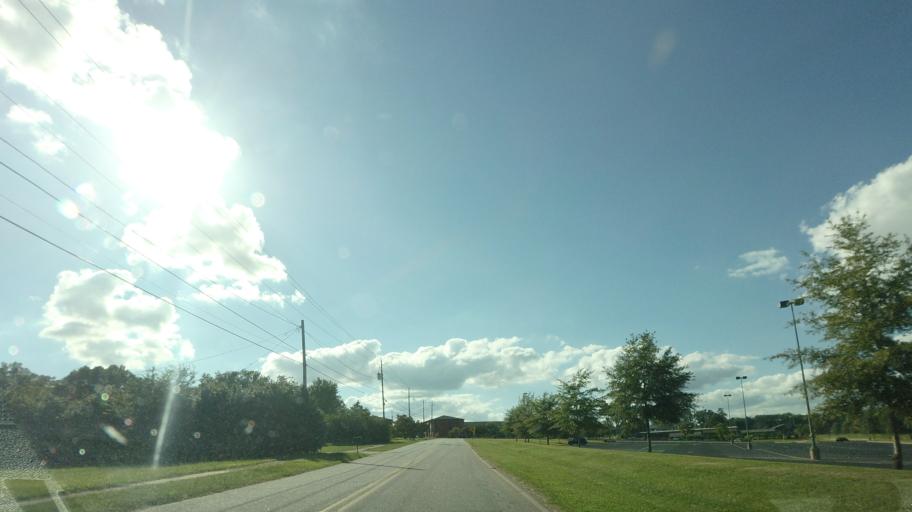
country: US
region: Georgia
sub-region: Lamar County
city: Barnesville
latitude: 33.0444
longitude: -84.1476
